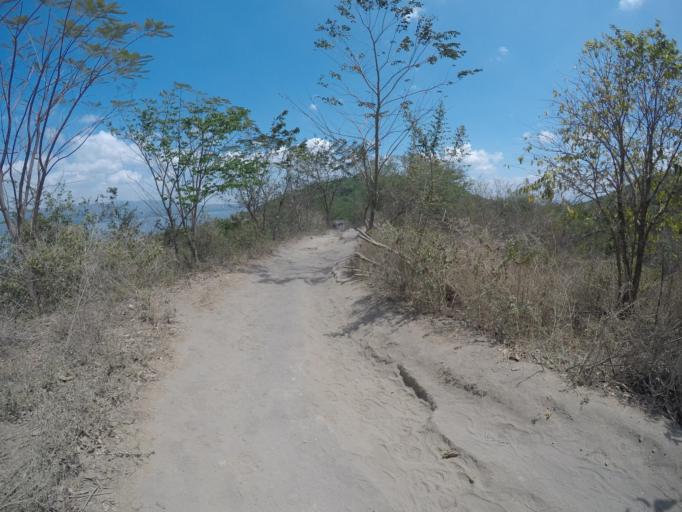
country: PH
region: Calabarzon
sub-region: Province of Batangas
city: Bugaan
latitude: 14.0246
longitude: 120.9991
